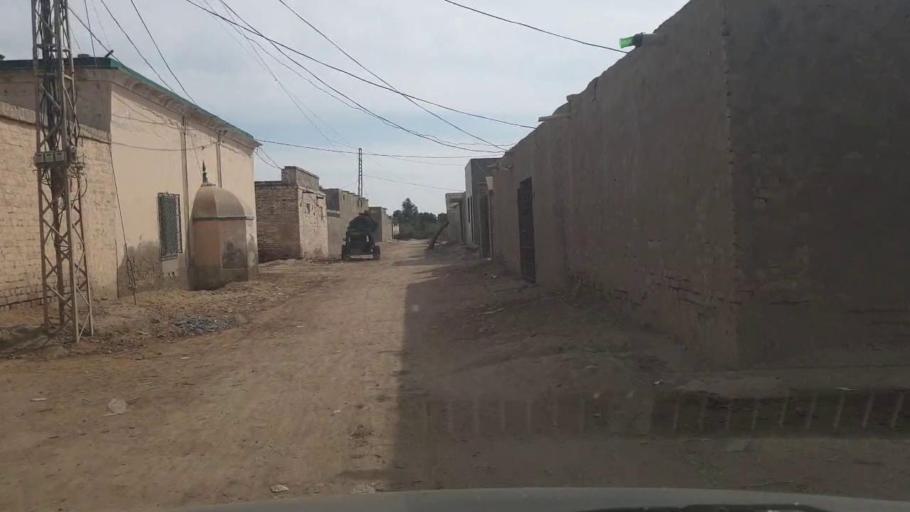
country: PK
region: Sindh
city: Kunri
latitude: 25.2378
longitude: 69.5896
